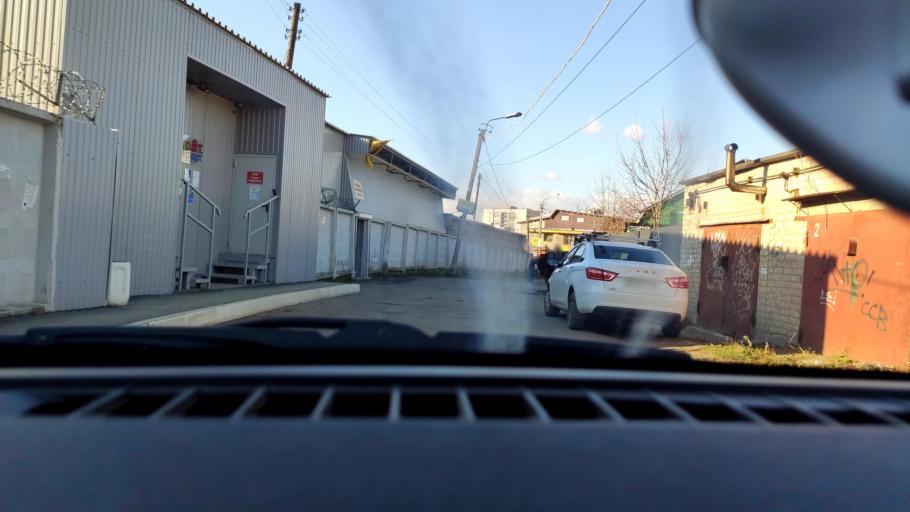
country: RU
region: Perm
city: Perm
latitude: 57.9801
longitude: 56.2408
